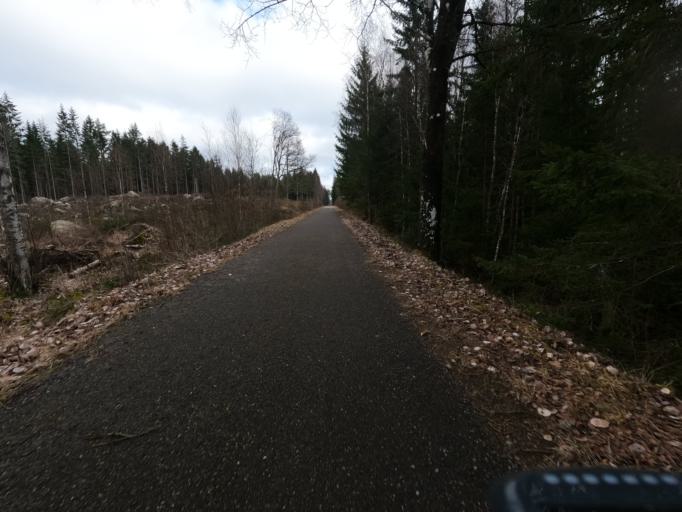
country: SE
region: Joenkoeping
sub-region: Varnamo Kommun
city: Rydaholm
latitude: 56.8463
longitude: 14.2146
